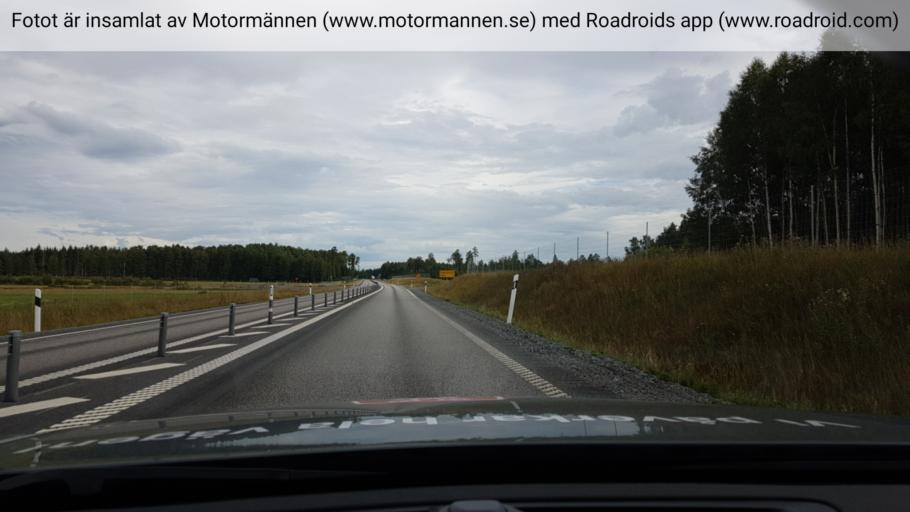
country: SE
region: Uppsala
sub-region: Heby Kommun
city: Heby
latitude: 60.0312
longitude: 16.8695
